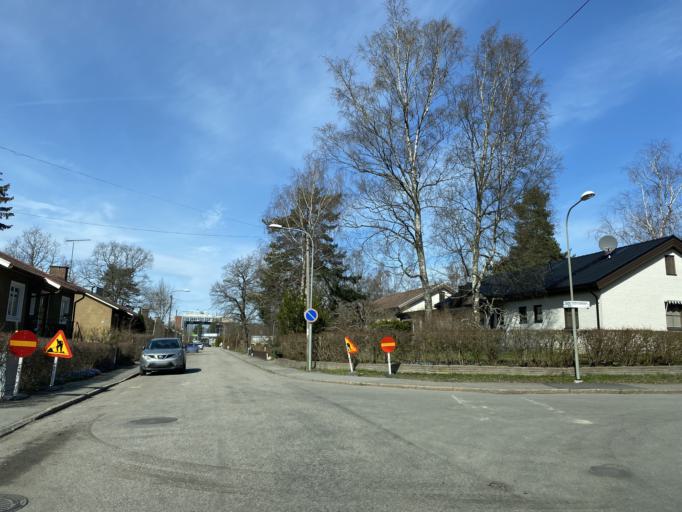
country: SE
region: Stockholm
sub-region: Stockholms Kommun
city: Arsta
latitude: 59.2870
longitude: 18.0140
